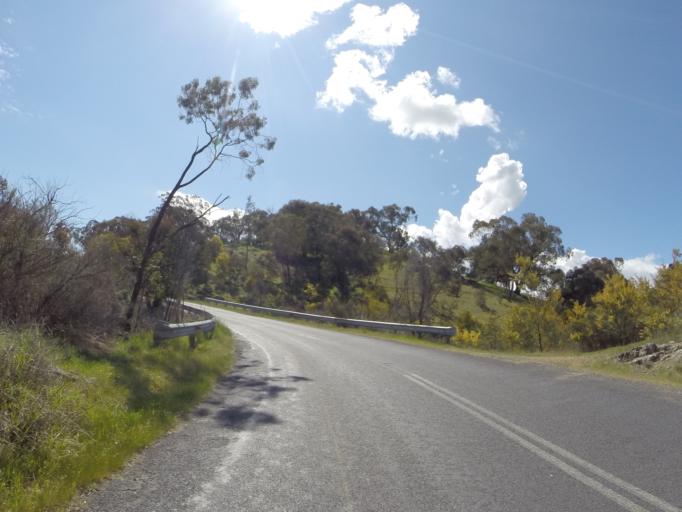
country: AU
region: New South Wales
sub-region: Yass Valley
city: Yass
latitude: -34.9917
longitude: 148.8430
